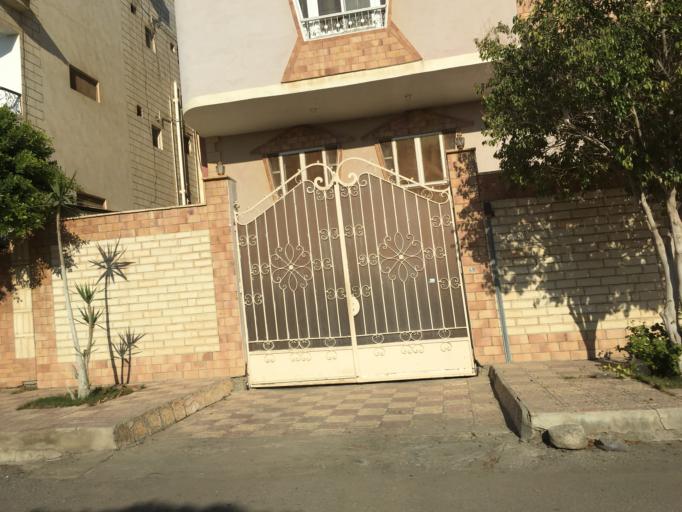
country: EG
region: Al Jizah
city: Madinat Sittah Uktubar
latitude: 29.9867
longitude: 30.9426
